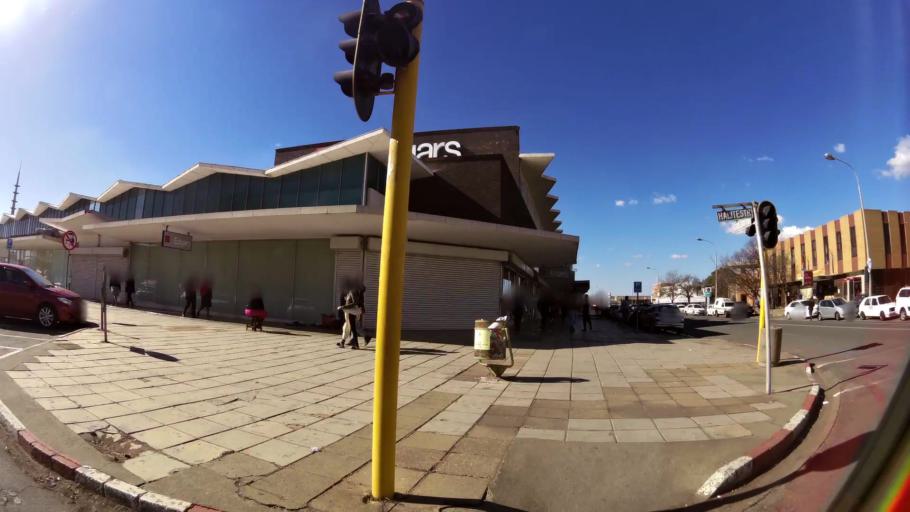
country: ZA
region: Gauteng
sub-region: West Rand District Municipality
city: Carletonville
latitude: -26.3580
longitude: 27.3980
